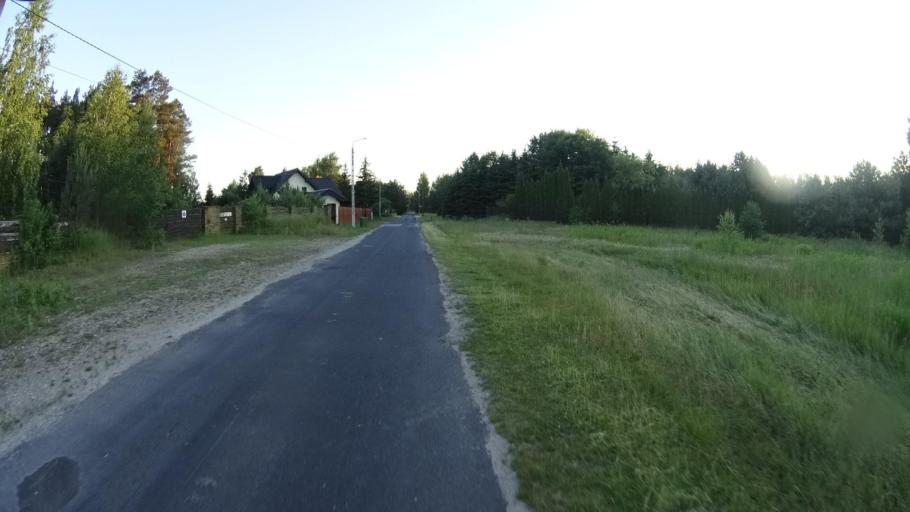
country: PL
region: Masovian Voivodeship
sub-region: Powiat warszawski zachodni
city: Truskaw
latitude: 52.2764
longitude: 20.7047
